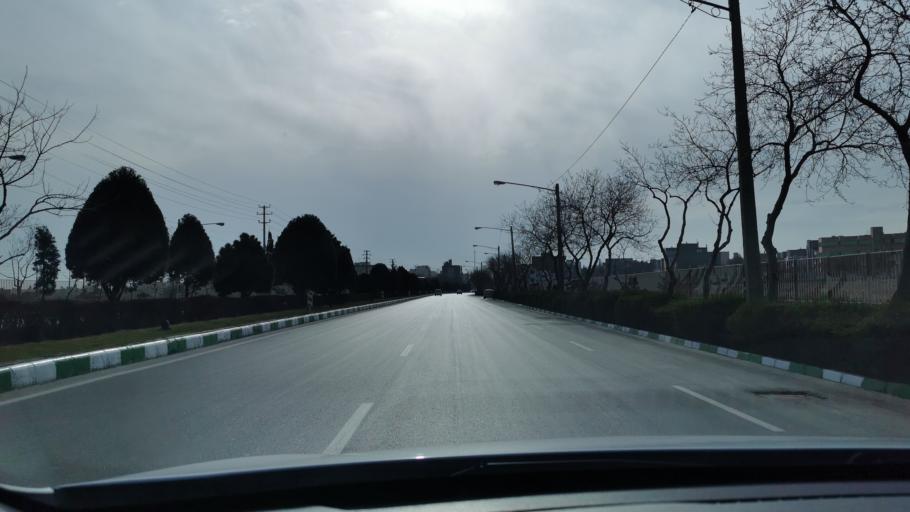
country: IR
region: Razavi Khorasan
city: Mashhad
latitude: 36.3007
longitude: 59.5205
